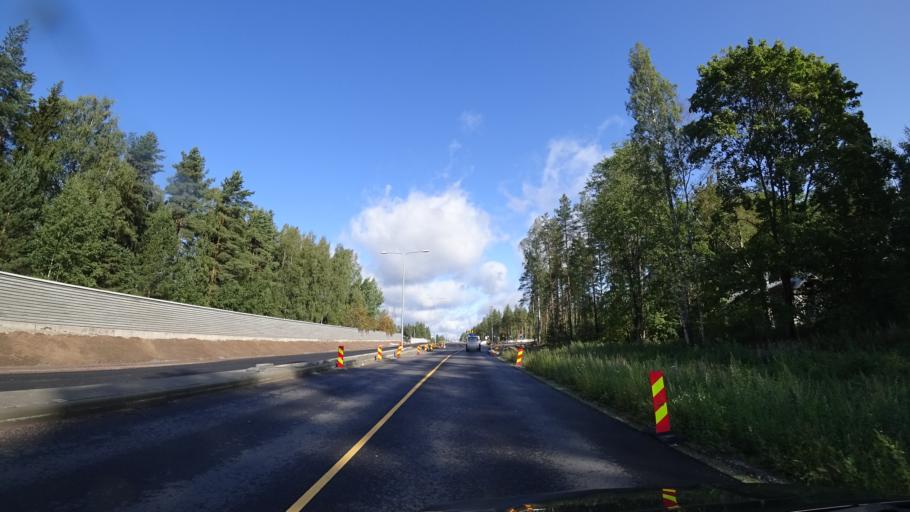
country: FI
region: Uusimaa
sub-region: Helsinki
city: Tuusula
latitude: 60.4095
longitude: 25.0053
